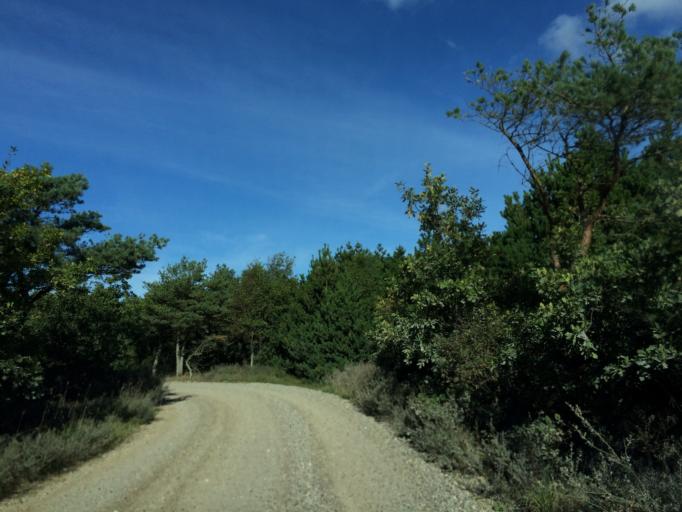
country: DK
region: Central Jutland
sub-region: Holstebro Kommune
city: Ulfborg
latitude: 56.2869
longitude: 8.1469
